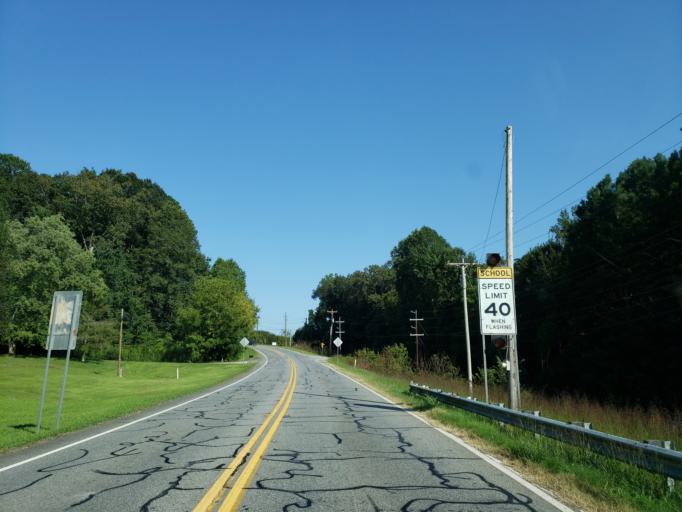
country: US
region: Georgia
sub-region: Catoosa County
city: Ringgold
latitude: 34.9054
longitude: -85.0756
